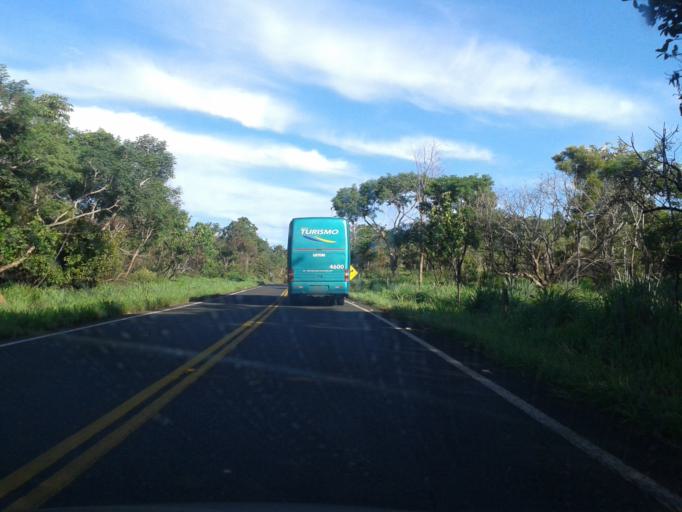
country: BR
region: Minas Gerais
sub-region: Tupaciguara
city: Tupaciguara
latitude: -18.3040
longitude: -48.5617
